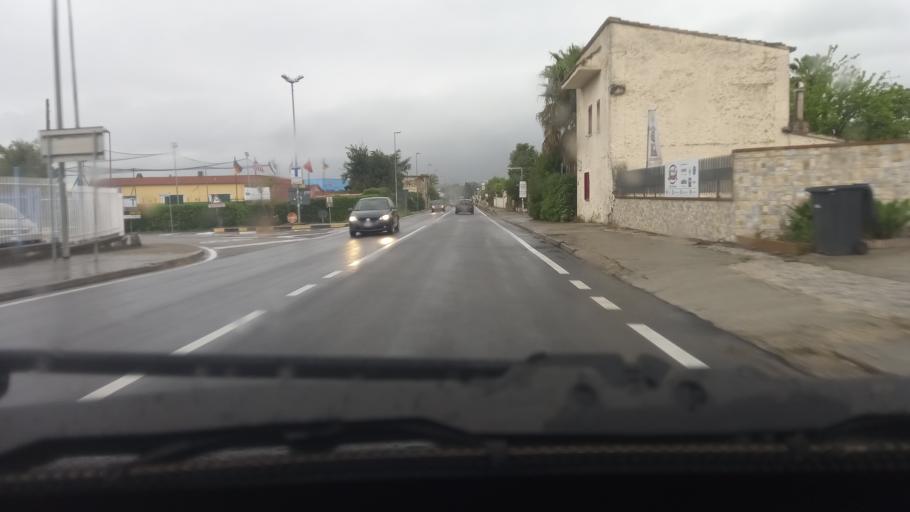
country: IT
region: Latium
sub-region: Provincia di Latina
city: Penitro
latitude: 41.2615
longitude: 13.6869
